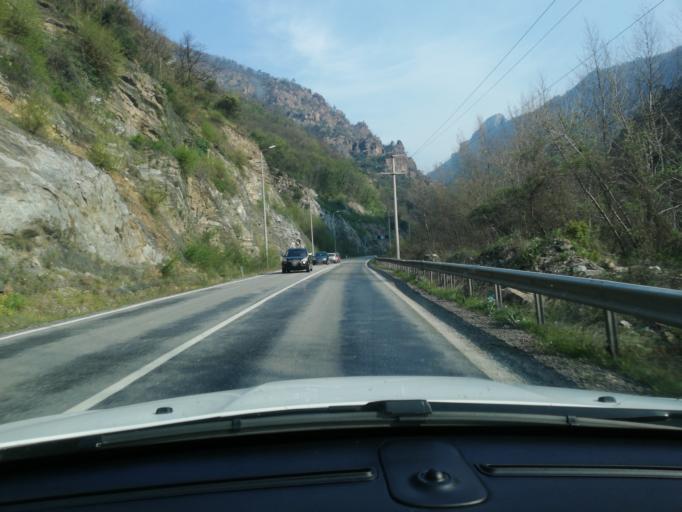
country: TR
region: Karabuk
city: Yenice
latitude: 41.1735
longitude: 32.4466
